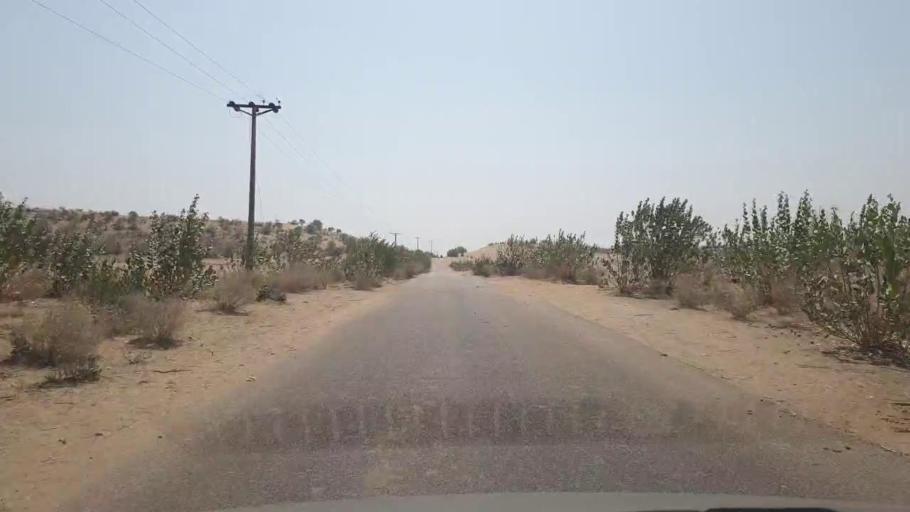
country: PK
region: Sindh
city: Chor
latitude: 25.6193
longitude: 70.1760
